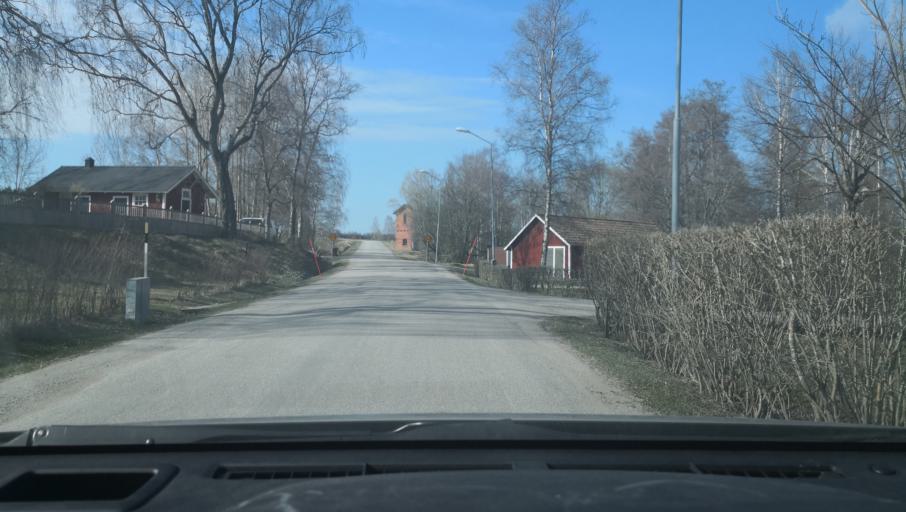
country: SE
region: Uppsala
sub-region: Heby Kommun
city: Morgongava
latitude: 59.8422
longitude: 16.9158
